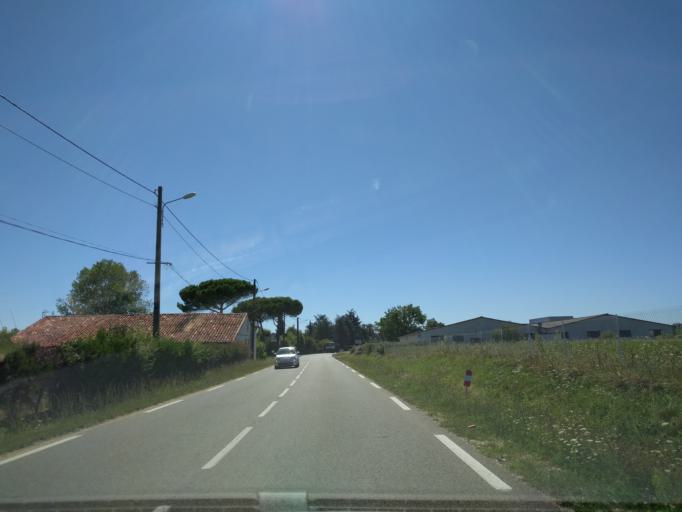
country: FR
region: Midi-Pyrenees
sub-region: Departement du Tarn-et-Garonne
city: Montauban
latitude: 44.0270
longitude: 1.3799
